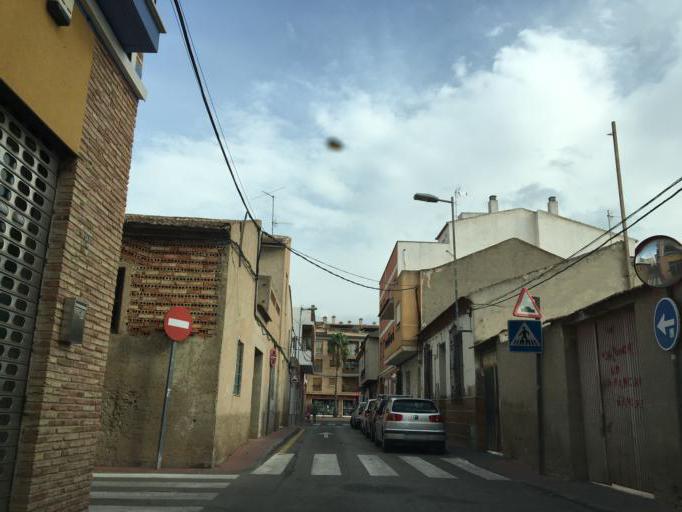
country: ES
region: Murcia
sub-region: Murcia
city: Murcia
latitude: 38.0054
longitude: -1.0734
